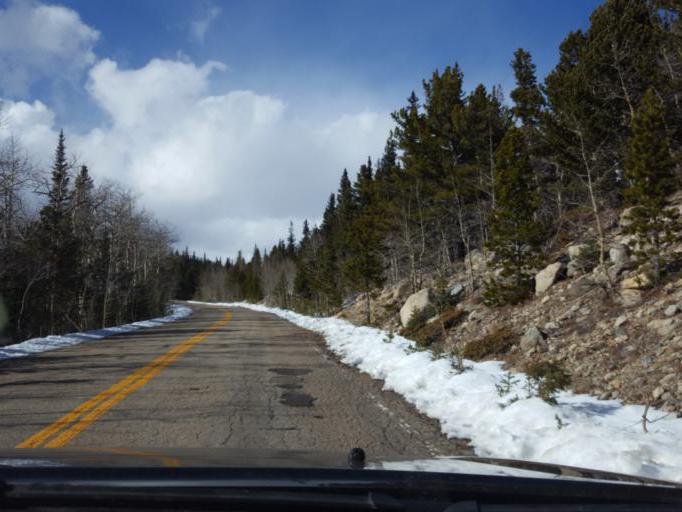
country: US
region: Colorado
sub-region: Boulder County
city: Nederland
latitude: 40.0791
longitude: -105.5318
